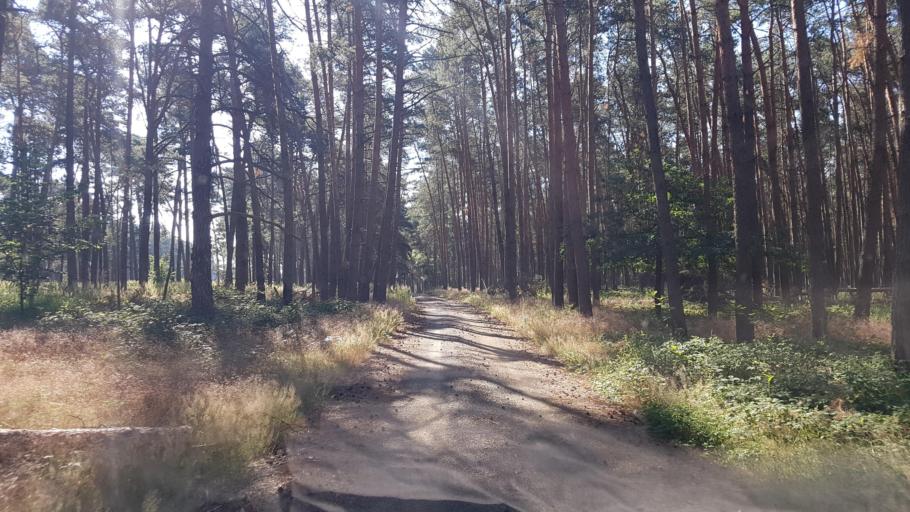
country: DE
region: Brandenburg
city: Juterbog
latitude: 51.9511
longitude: 13.1937
